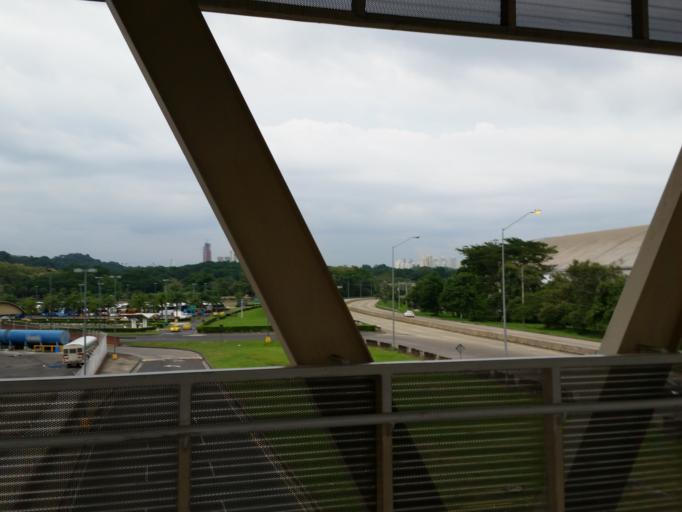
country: PA
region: Panama
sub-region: Distrito de Panama
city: Ancon
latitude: 8.9739
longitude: -79.5504
